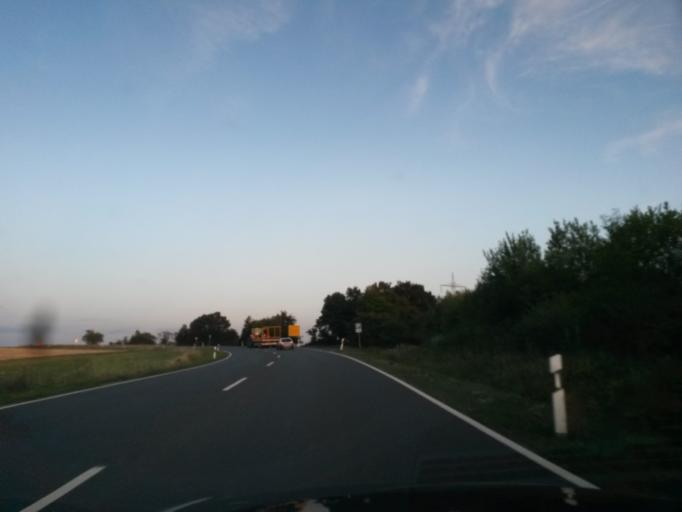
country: DE
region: Bavaria
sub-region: Regierungsbezirk Unterfranken
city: Holzkirchen
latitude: 49.8062
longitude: 9.6477
